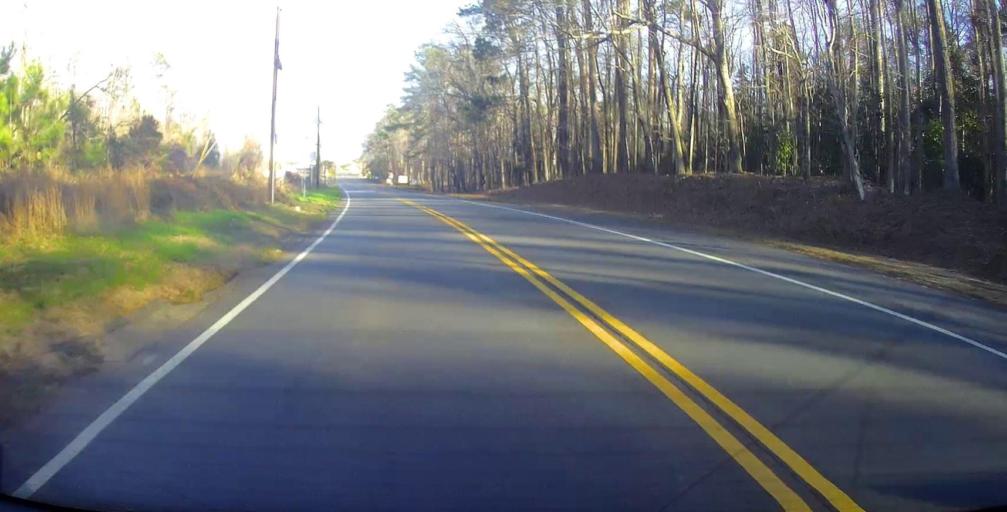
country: US
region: Georgia
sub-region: Meriwether County
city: Manchester
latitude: 32.8916
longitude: -84.6872
